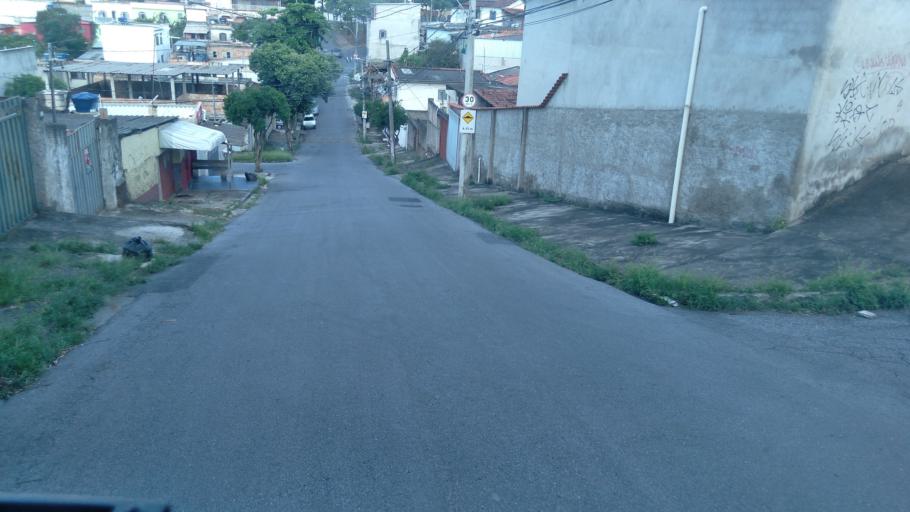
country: BR
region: Minas Gerais
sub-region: Belo Horizonte
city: Belo Horizonte
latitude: -19.8513
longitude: -43.9121
